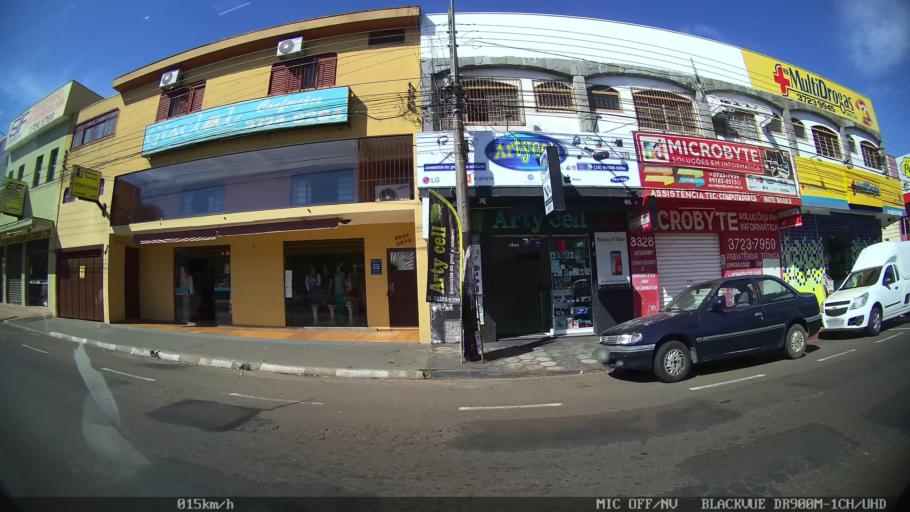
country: BR
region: Sao Paulo
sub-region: Franca
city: Franca
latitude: -20.5219
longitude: -47.4097
